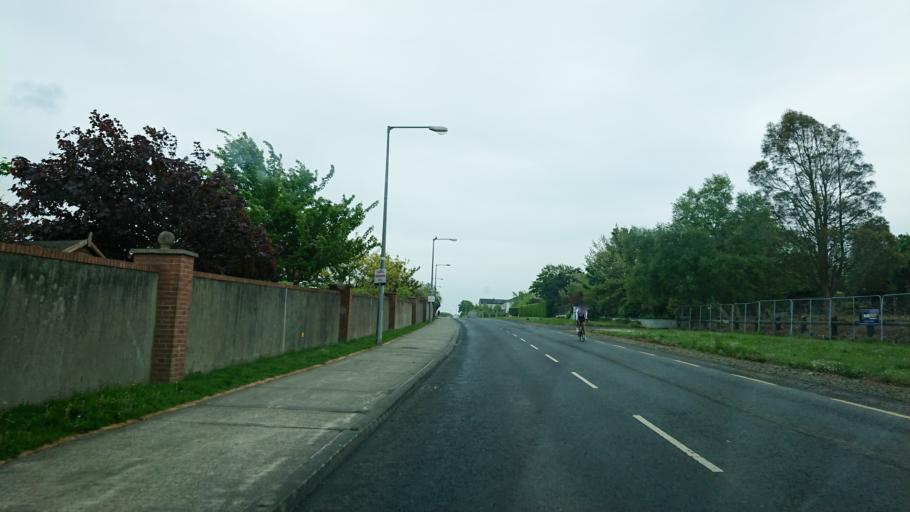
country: IE
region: Munster
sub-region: Waterford
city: Waterford
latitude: 52.2307
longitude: -7.0668
